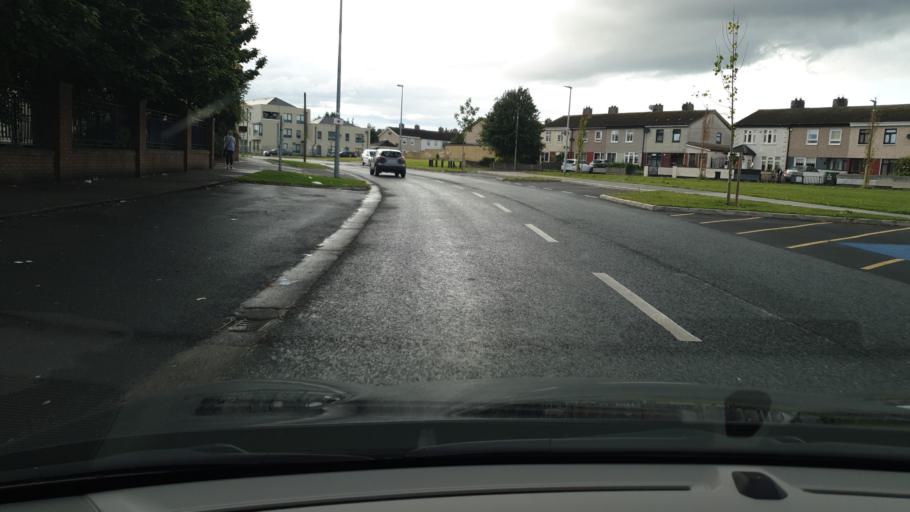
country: IE
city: Palmerstown
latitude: 53.3444
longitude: -6.3951
